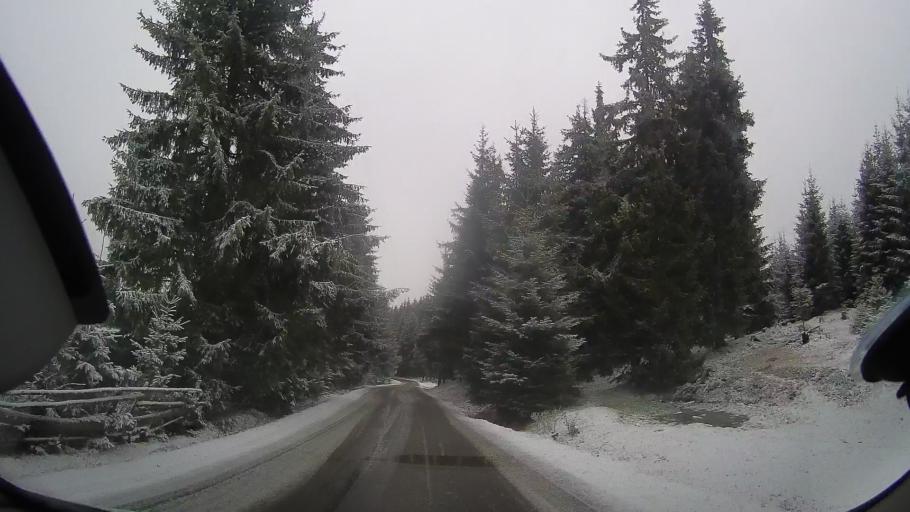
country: RO
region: Cluj
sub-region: Comuna Belis
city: Belis
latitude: 46.6448
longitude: 23.0662
